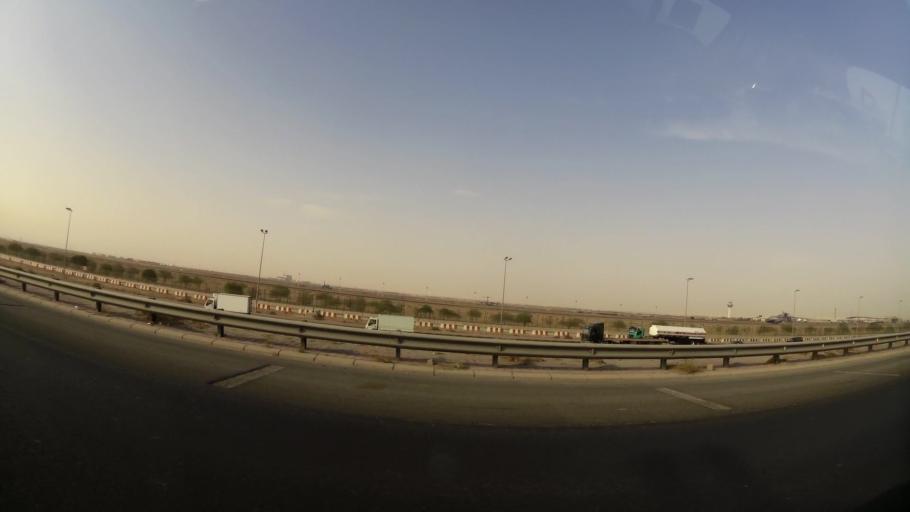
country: KW
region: Al Farwaniyah
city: Janub as Surrah
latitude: 29.2208
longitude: 47.9985
